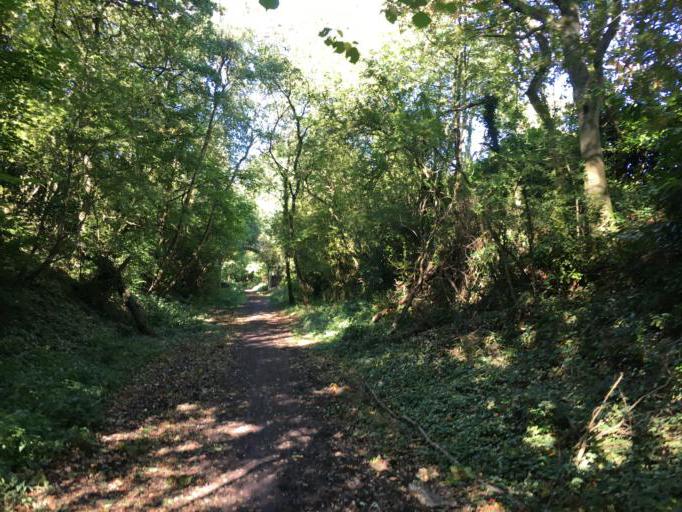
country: GB
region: England
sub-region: Warwickshire
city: Kenilworth
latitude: 52.3799
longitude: -1.6052
